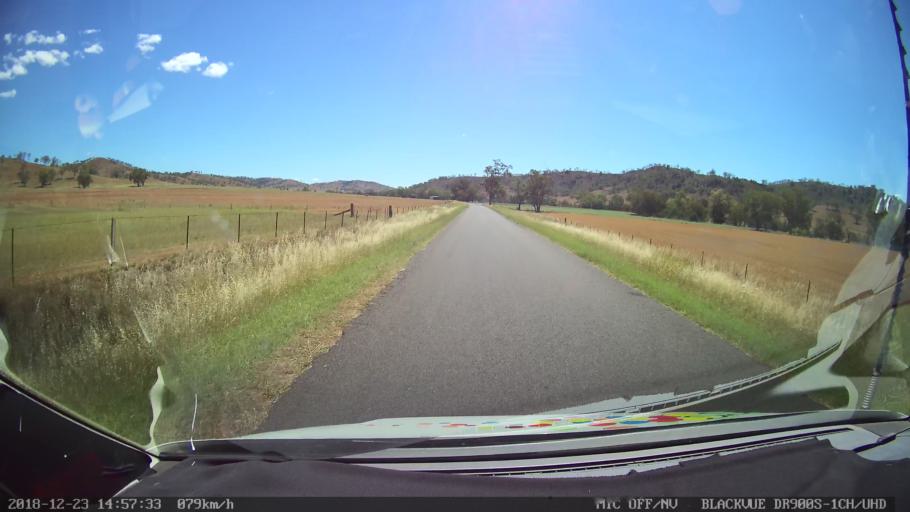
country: AU
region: New South Wales
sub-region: Tamworth Municipality
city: Manilla
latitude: -30.7103
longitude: 150.8235
